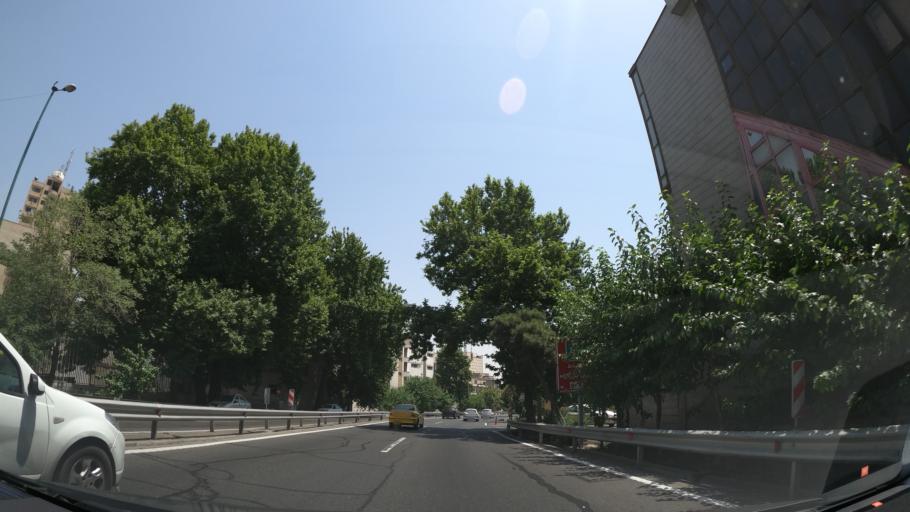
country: IR
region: Tehran
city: Tehran
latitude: 35.7211
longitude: 51.4262
